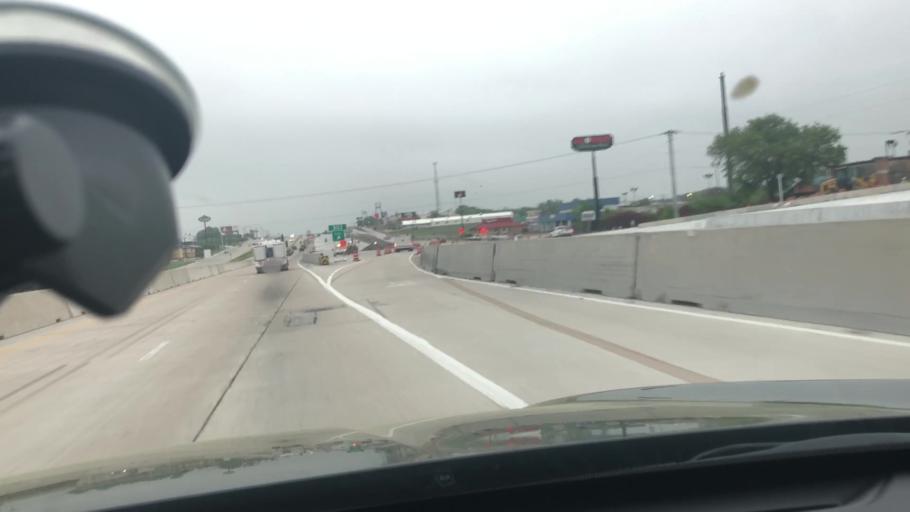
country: US
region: Texas
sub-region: Bell County
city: Temple
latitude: 31.1043
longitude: -97.3590
